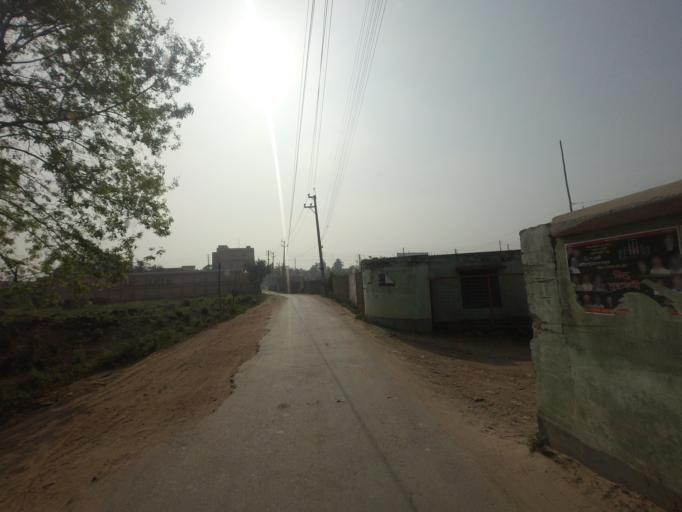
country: BD
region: Dhaka
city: Paltan
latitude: 23.7873
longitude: 90.5705
